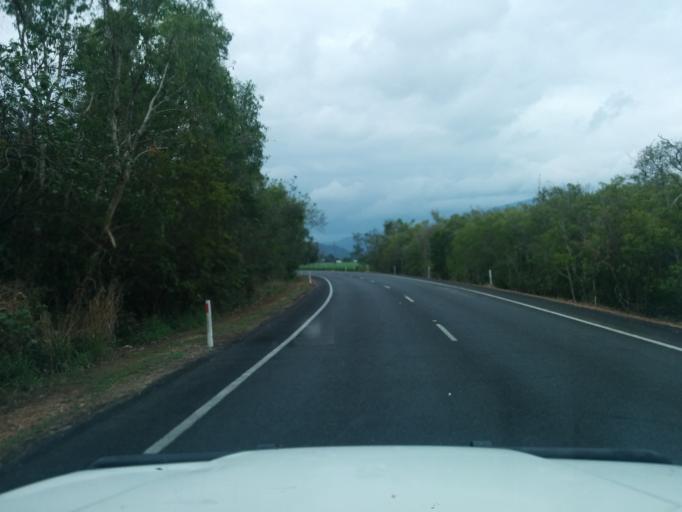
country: AU
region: Queensland
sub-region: Cairns
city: Yorkeys Knob
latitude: -16.8487
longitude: 145.7341
